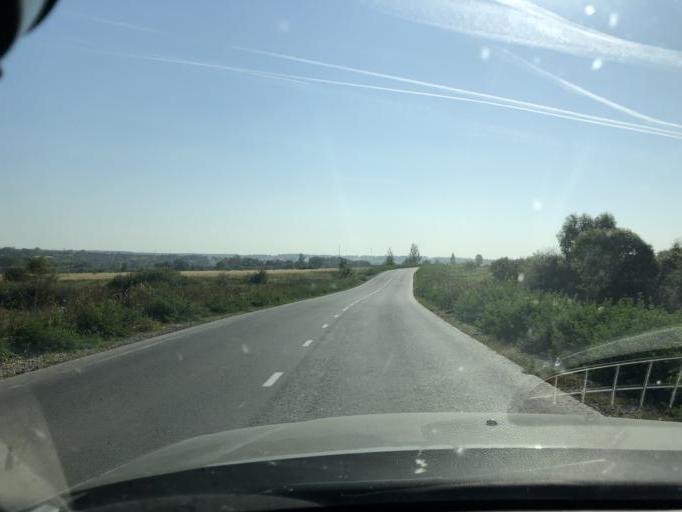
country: RU
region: Tula
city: Yasnogorsk
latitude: 54.4690
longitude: 37.6742
